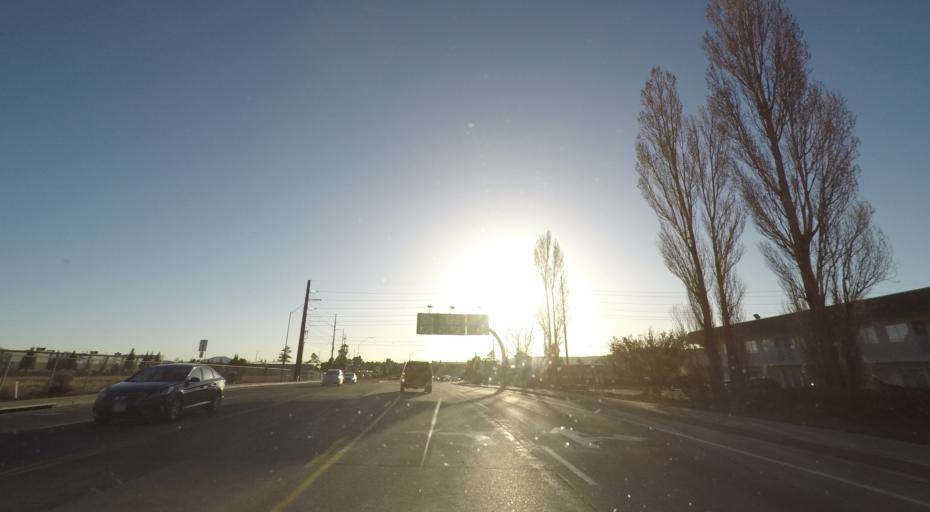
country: US
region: Arizona
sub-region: Coconino County
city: Flagstaff
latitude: 35.1922
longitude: -111.6255
